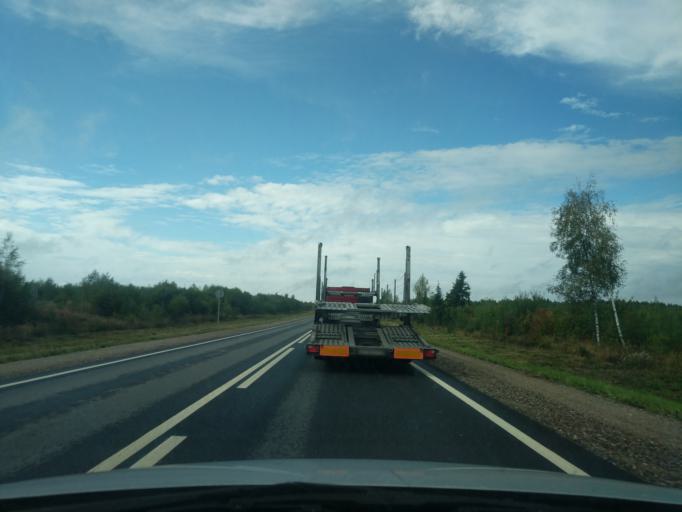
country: RU
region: Kostroma
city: Sudislavl'
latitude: 57.8200
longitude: 41.9212
